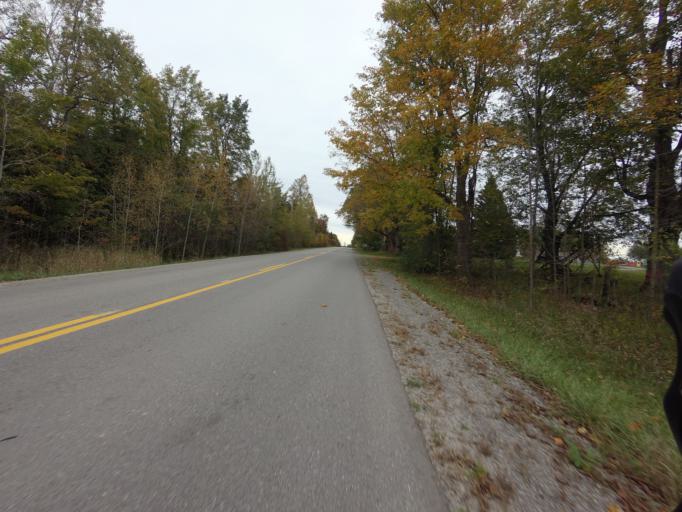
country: CA
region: Ontario
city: Brockville
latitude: 44.7610
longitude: -75.7668
